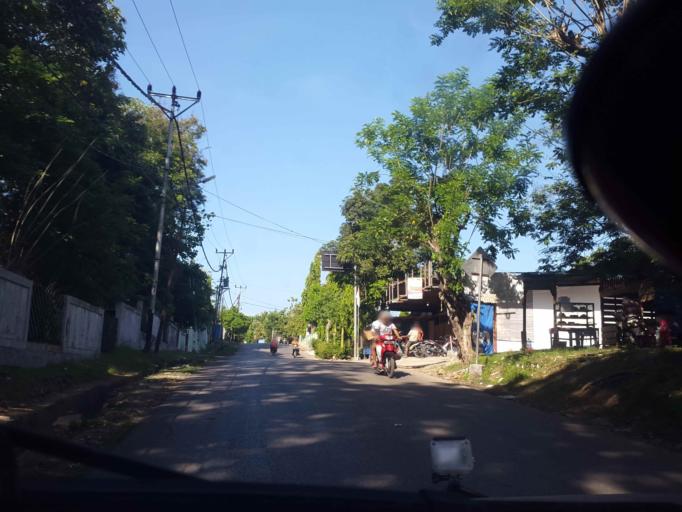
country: ID
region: East Nusa Tenggara
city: Airnona
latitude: -10.1794
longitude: 123.5911
